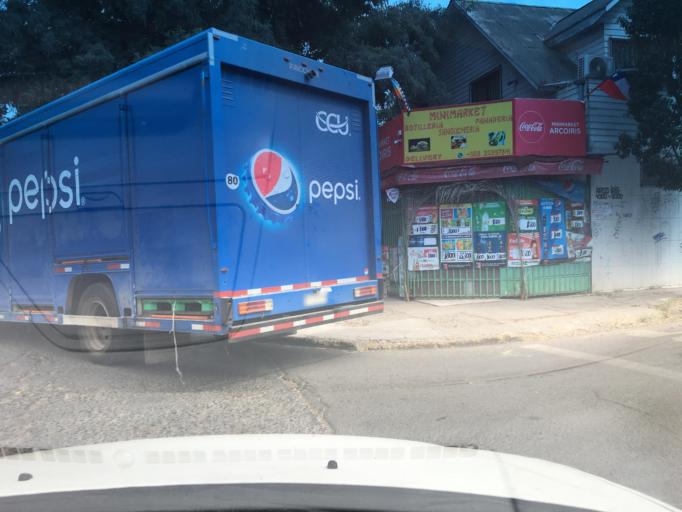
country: CL
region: Santiago Metropolitan
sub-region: Provincia de Santiago
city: Santiago
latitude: -33.3868
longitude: -70.6459
